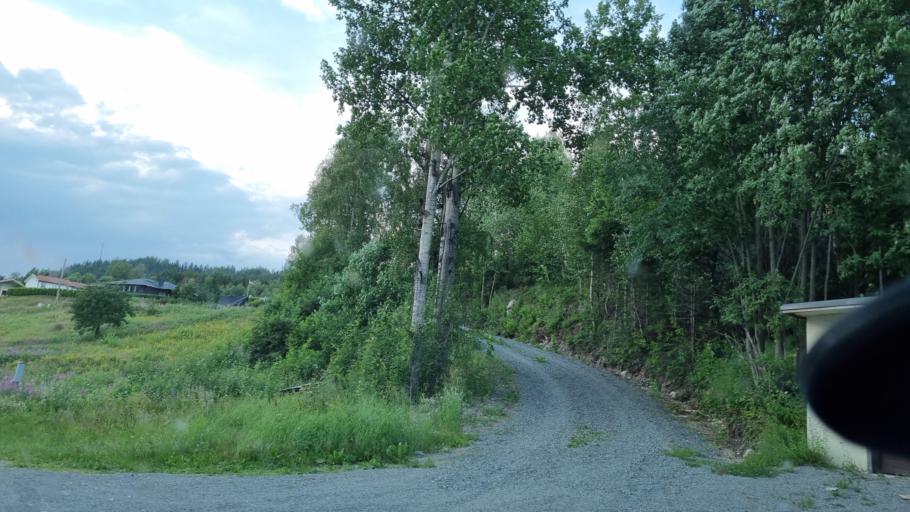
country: NO
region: Hedmark
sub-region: Trysil
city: Innbygda
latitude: 61.3228
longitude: 12.2578
